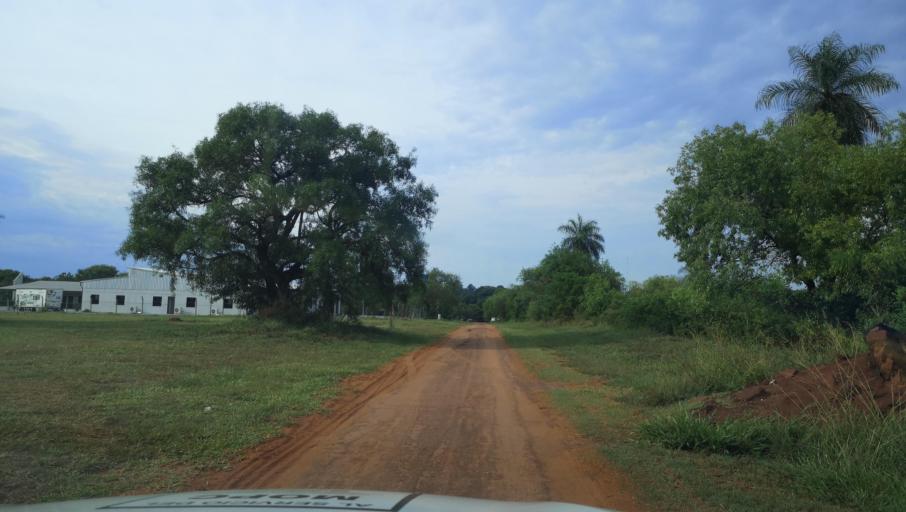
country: PY
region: Misiones
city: Santa Maria
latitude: -26.8795
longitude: -57.0342
